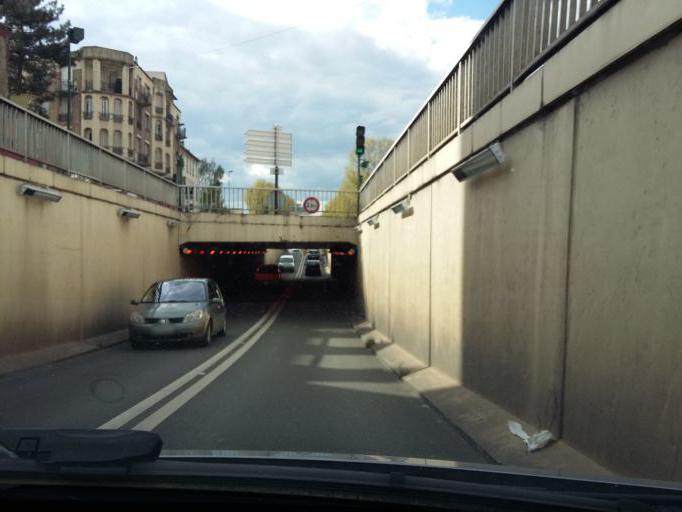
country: FR
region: Ile-de-France
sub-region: Departement du Val-d'Oise
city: Saint-Gratien
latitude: 48.9615
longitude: 2.2956
